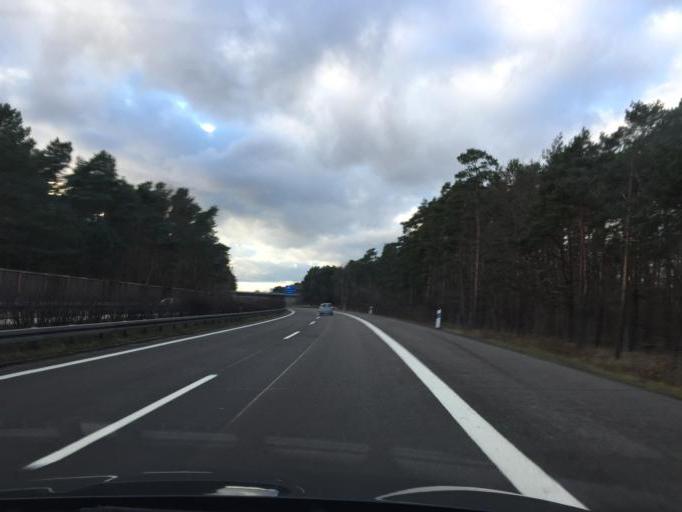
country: DE
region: Brandenburg
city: Lubbenau
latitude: 51.8394
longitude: 13.9564
